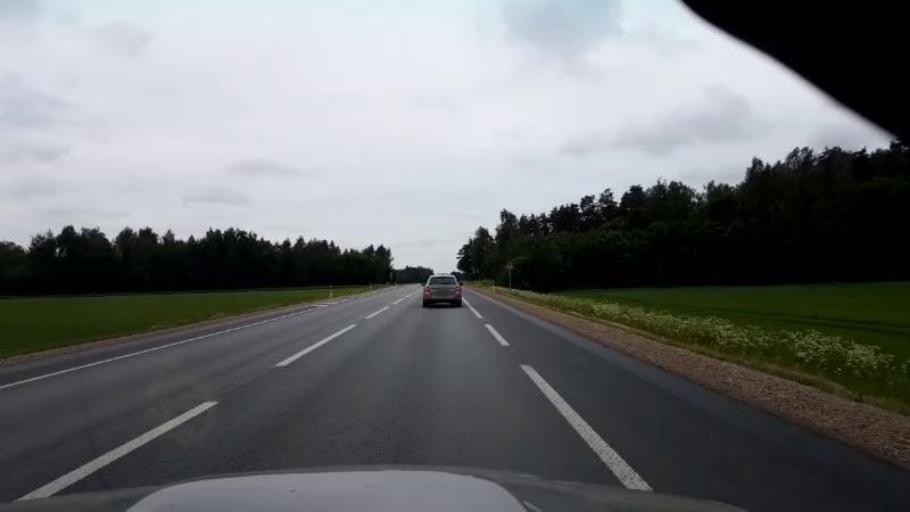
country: LV
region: Lecava
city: Iecava
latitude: 56.6529
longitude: 24.2299
